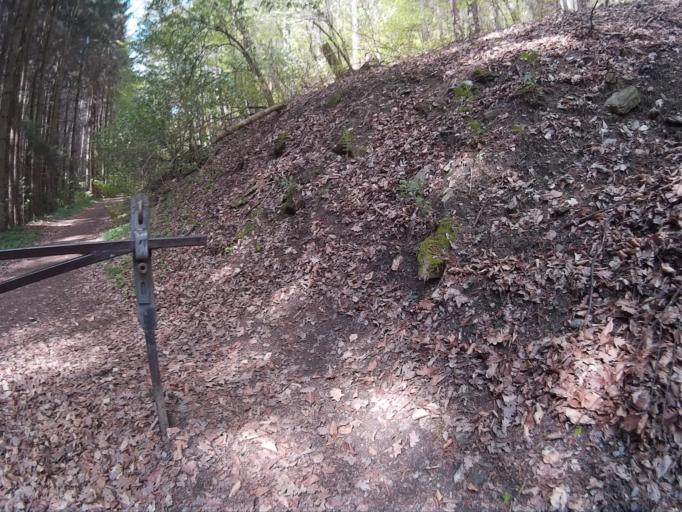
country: AT
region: Burgenland
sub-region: Politischer Bezirk Oberwart
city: Rechnitz
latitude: 47.3476
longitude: 16.4786
